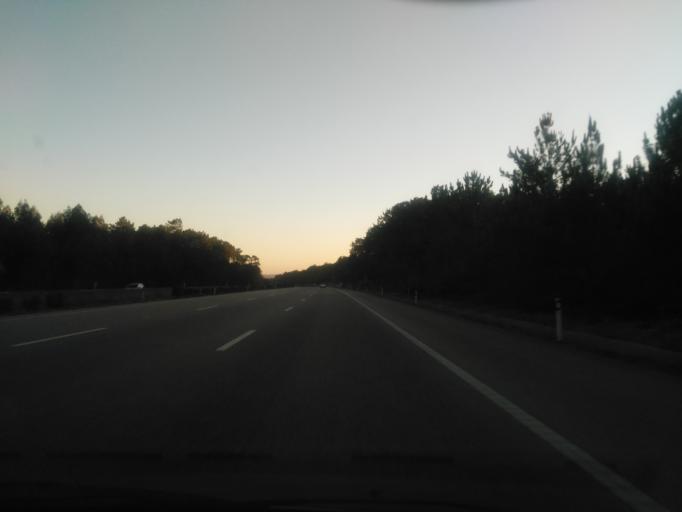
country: PT
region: Leiria
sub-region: Alcobaca
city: Pataias
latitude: 39.6667
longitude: -8.9540
